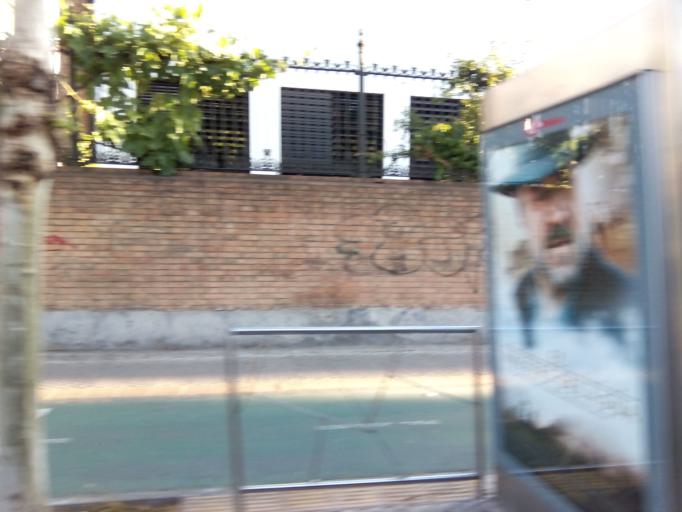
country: ES
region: Andalusia
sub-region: Provincia de Sevilla
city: Sevilla
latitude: 37.4034
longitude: -5.9923
